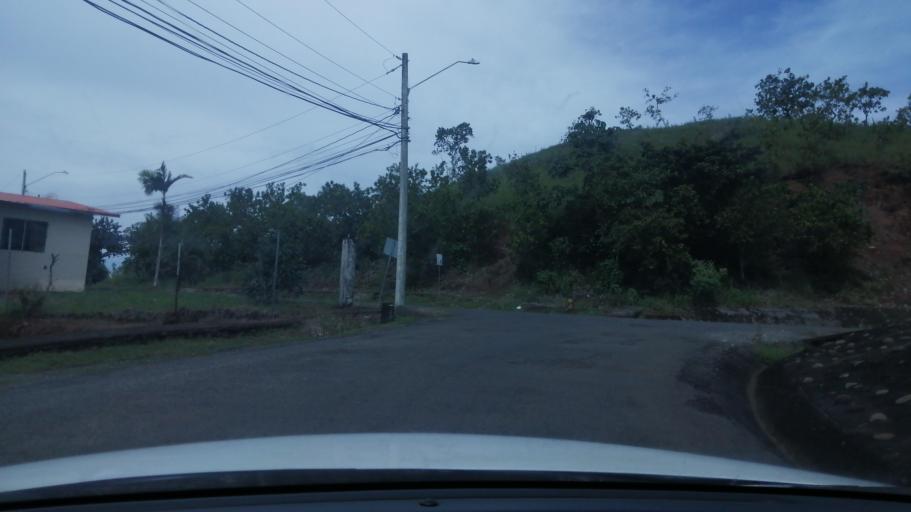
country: PA
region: Chiriqui
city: David
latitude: 8.4070
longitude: -82.4399
